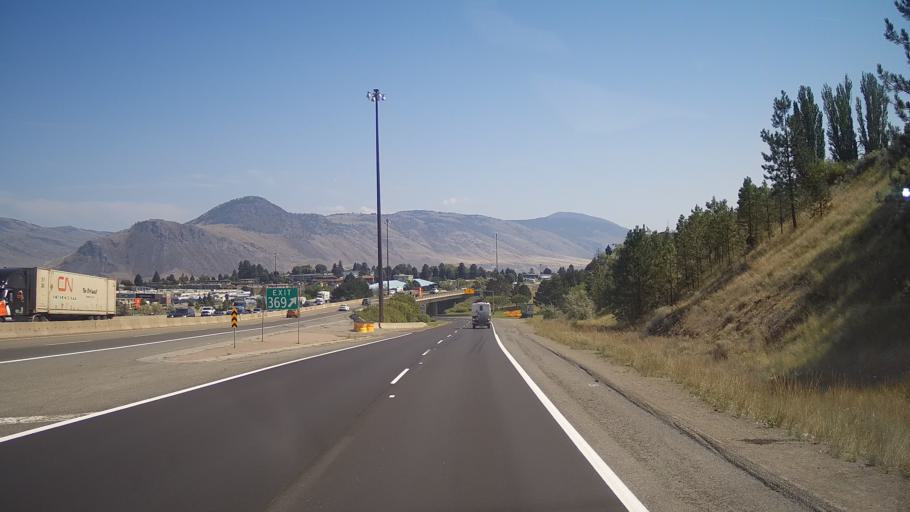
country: CA
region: British Columbia
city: Kamloops
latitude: 50.6598
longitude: -120.3585
